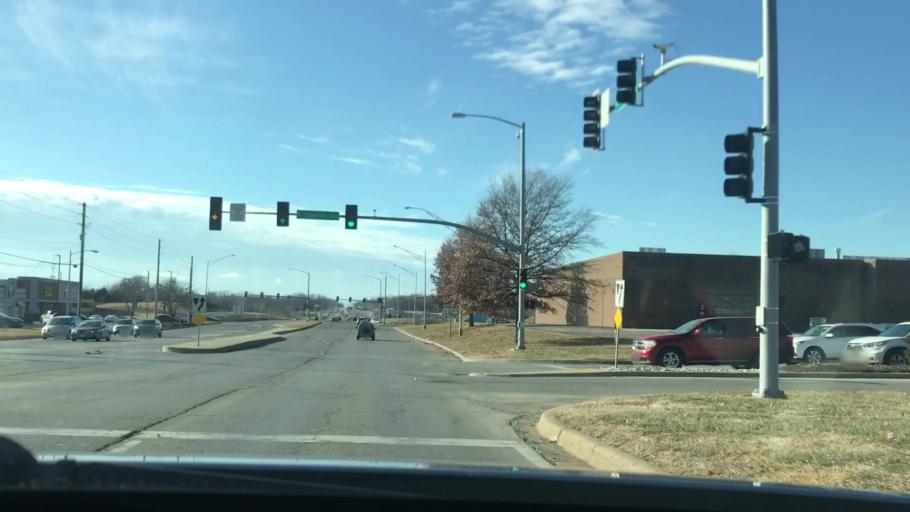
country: US
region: Missouri
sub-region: Clay County
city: Gladstone
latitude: 39.2465
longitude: -94.5873
